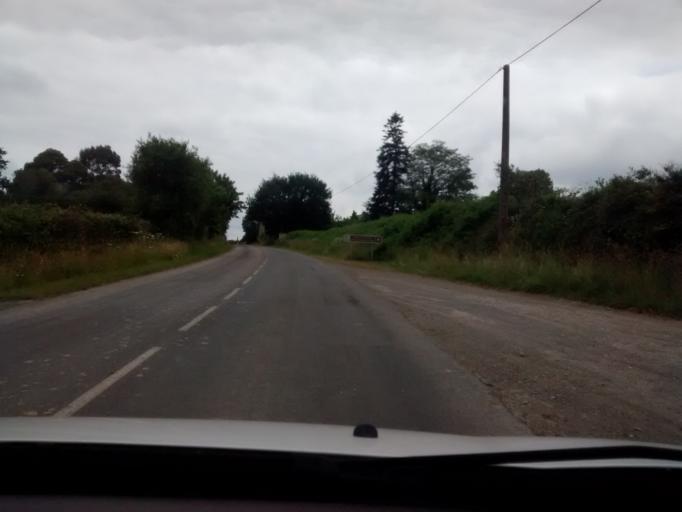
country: FR
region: Brittany
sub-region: Departement d'Ille-et-Vilaine
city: La Bouexiere
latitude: 48.1921
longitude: -1.4538
